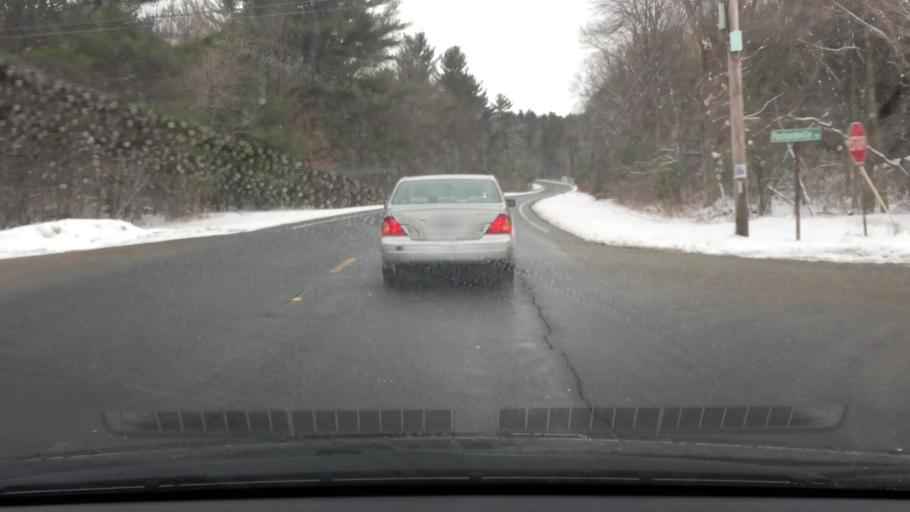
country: US
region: Massachusetts
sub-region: Hampshire County
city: Pelham
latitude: 42.3516
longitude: -72.4030
